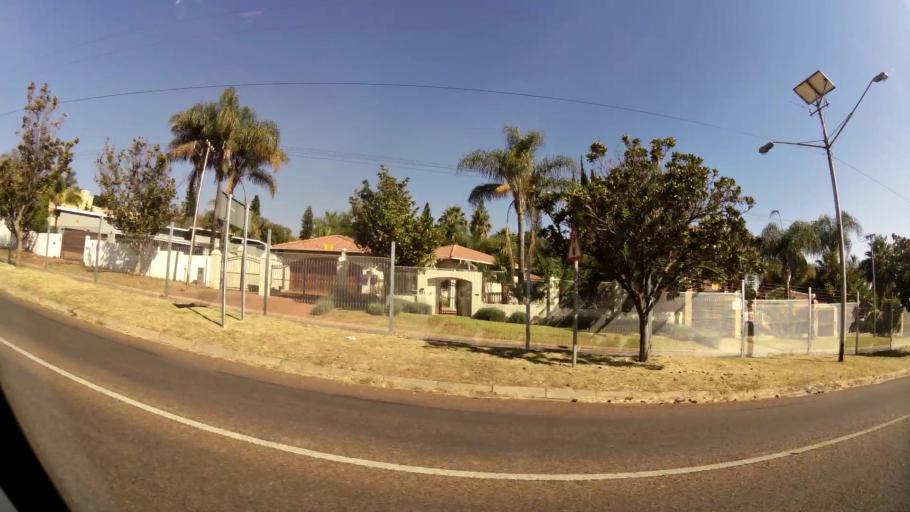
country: ZA
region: Gauteng
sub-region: City of Tshwane Metropolitan Municipality
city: Pretoria
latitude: -25.7784
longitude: 28.2265
